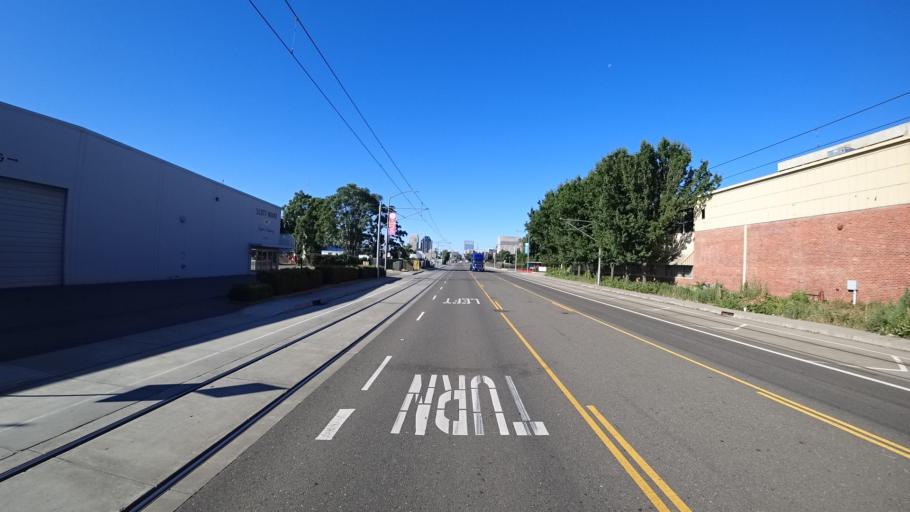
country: US
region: California
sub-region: Sacramento County
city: Sacramento
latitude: 38.5951
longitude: -121.4915
